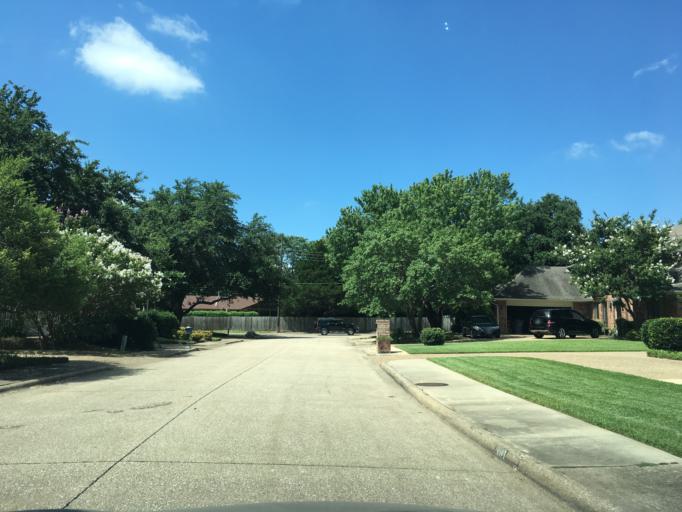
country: US
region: Texas
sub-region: Dallas County
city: Garland
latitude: 32.8385
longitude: -96.6479
